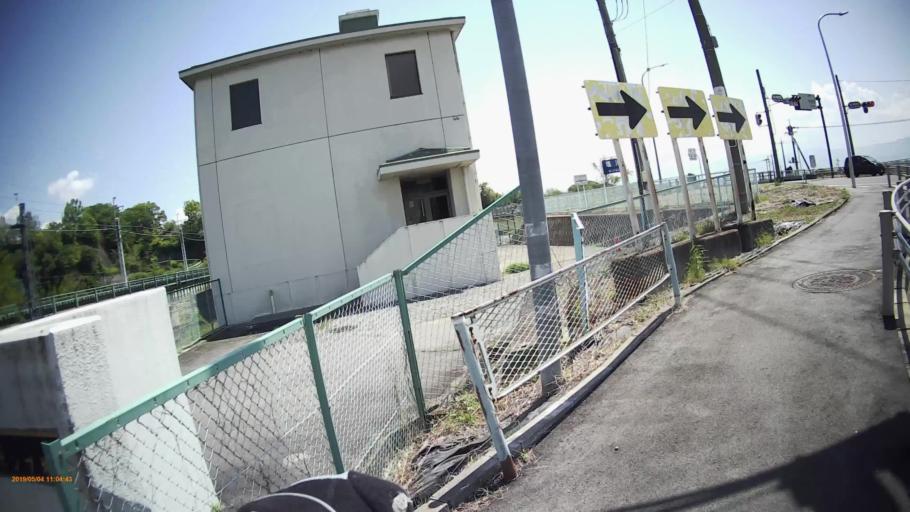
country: JP
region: Yamanashi
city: Nirasaki
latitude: 35.6983
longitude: 138.4661
